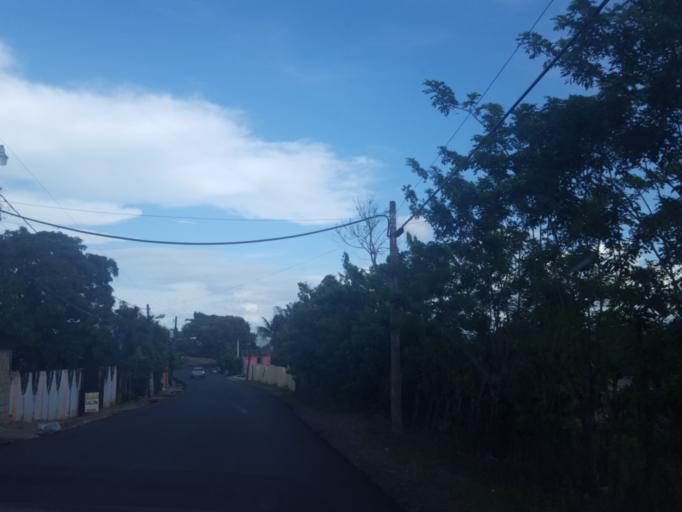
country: DO
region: La Vega
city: Rio Verde Arriba
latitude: 19.3514
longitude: -70.6279
